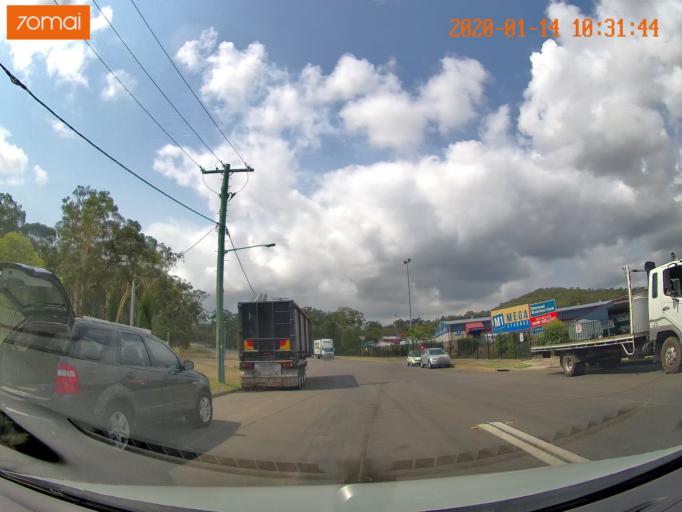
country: AU
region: New South Wales
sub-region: Lake Macquarie Shire
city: Dora Creek
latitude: -33.1205
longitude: 151.4709
